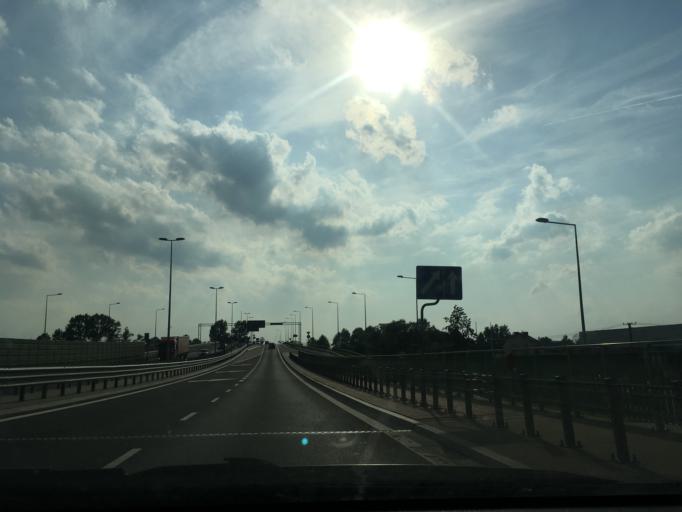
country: PL
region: Podlasie
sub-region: Powiat bialostocki
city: Dobrzyniewo Duze
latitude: 53.1528
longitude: 23.0757
